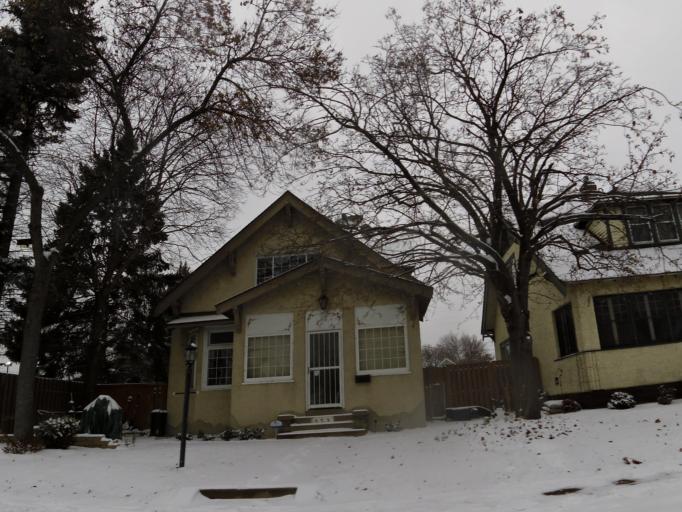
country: US
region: Minnesota
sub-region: Ramsey County
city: Saint Paul
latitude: 44.9776
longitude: -93.0645
